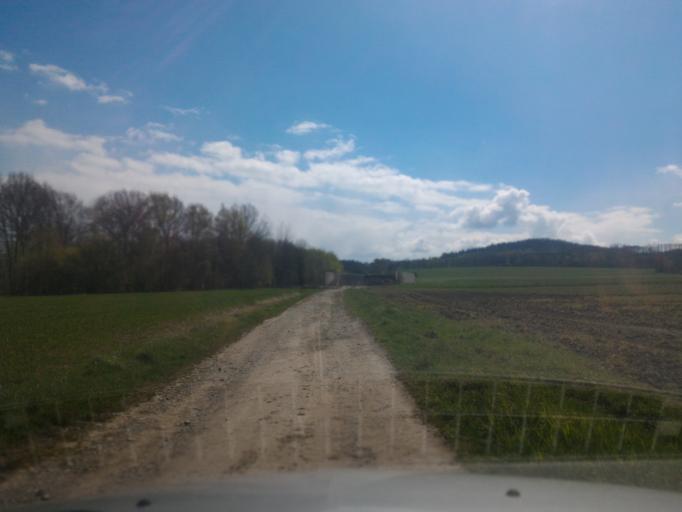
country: DE
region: Saxony
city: Leutersdorf
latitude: 50.9459
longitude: 14.6465
